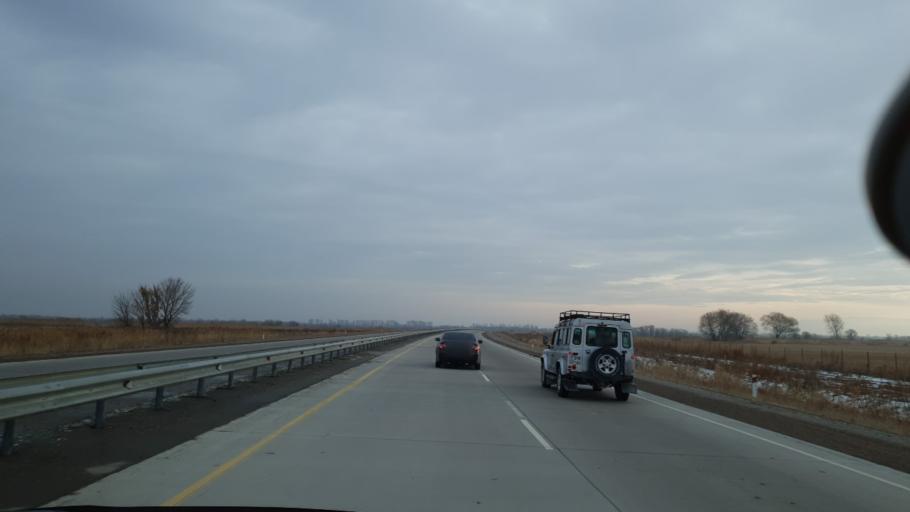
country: KZ
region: Almaty Oblysy
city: Esik
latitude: 43.5045
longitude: 77.3898
